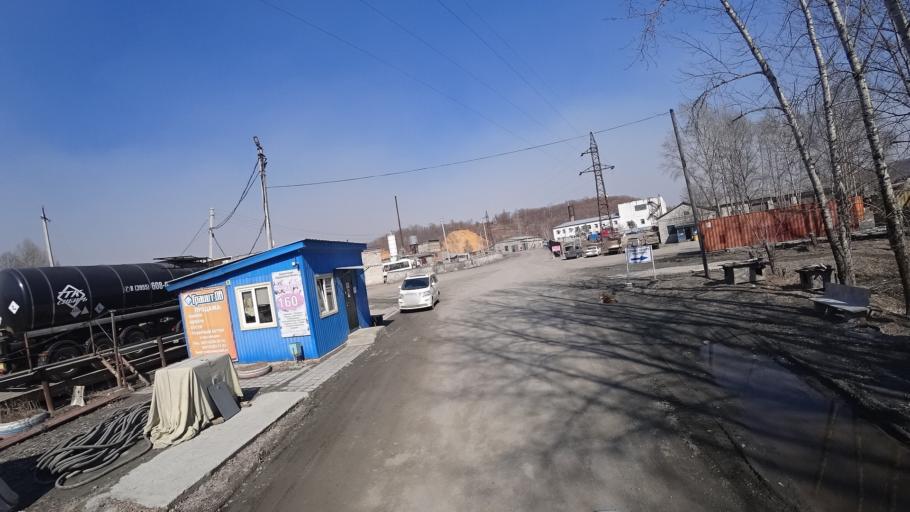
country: RU
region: Amur
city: Novobureyskiy
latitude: 49.7898
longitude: 129.9602
